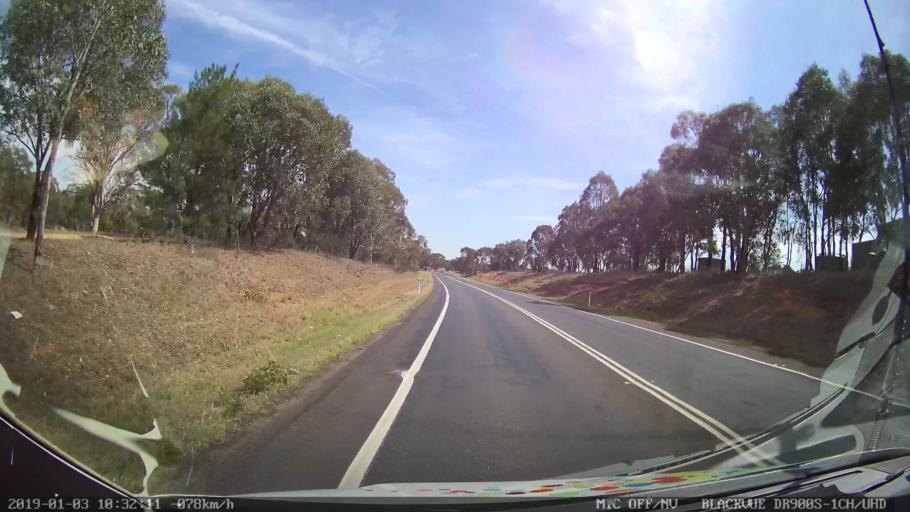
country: AU
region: New South Wales
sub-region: Young
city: Young
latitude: -34.3418
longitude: 148.2827
